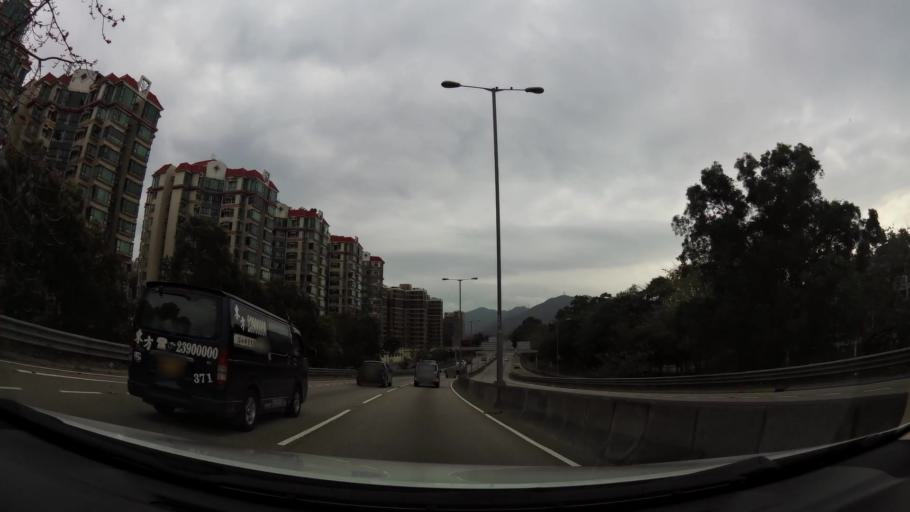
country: HK
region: Yuen Long
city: Yuen Long Kau Hui
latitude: 22.4432
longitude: 114.0168
